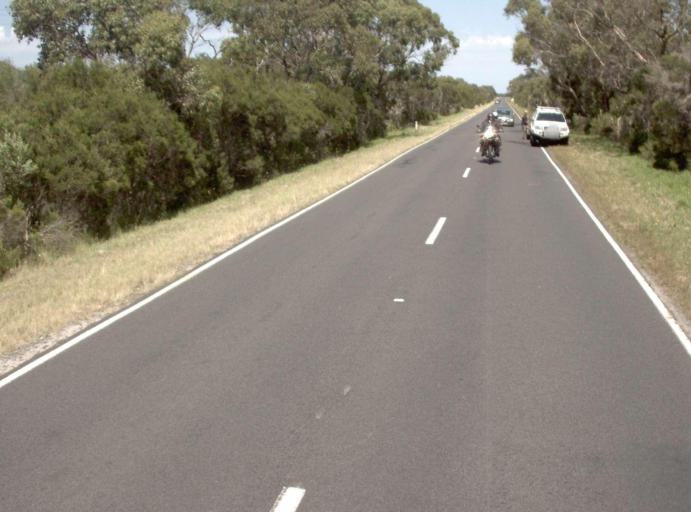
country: AU
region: Victoria
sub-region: Bass Coast
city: North Wonthaggi
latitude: -38.6291
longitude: 145.8059
